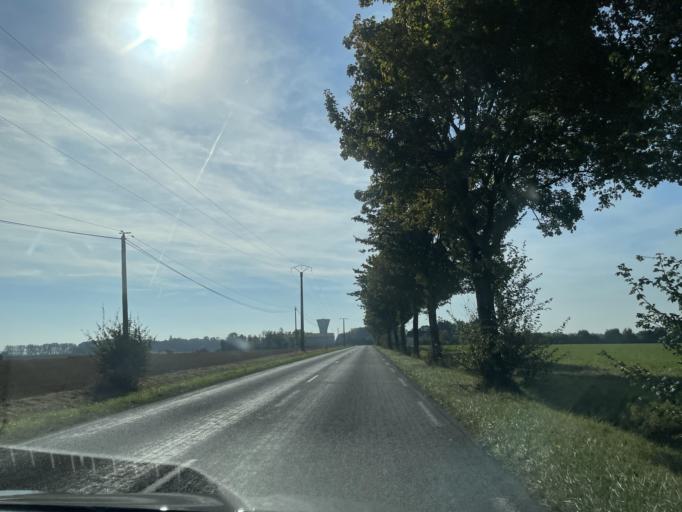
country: FR
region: Ile-de-France
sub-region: Departement de Seine-et-Marne
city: Coulommiers
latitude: 48.8522
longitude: 3.0904
